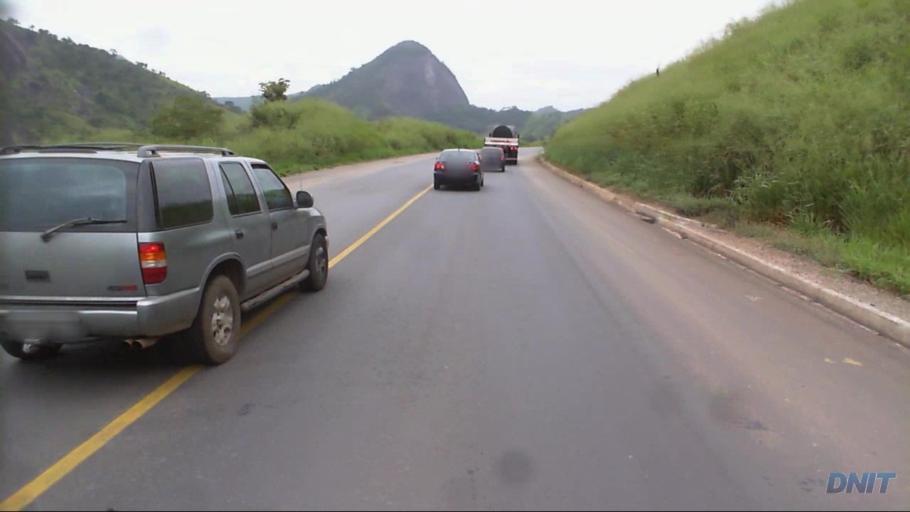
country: BR
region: Minas Gerais
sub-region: Timoteo
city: Timoteo
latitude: -19.5381
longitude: -42.6760
